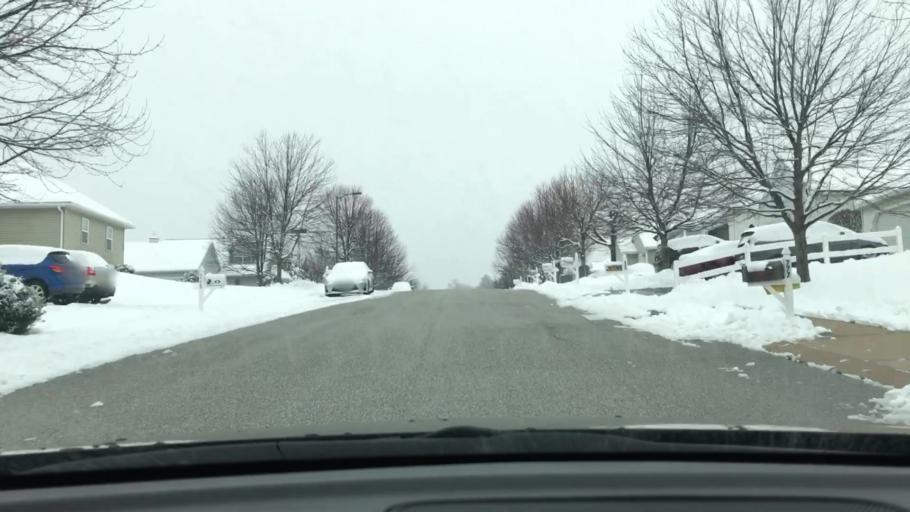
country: US
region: Pennsylvania
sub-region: York County
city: Yoe
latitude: 39.9099
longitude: -76.6494
